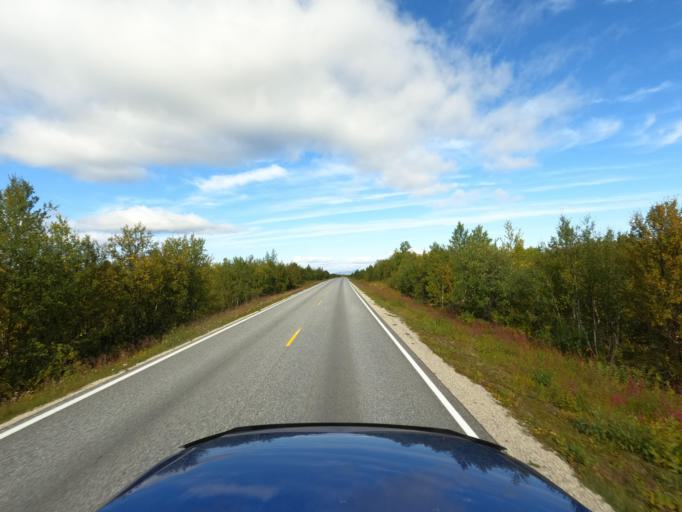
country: NO
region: Finnmark Fylke
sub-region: Karasjok
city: Karasjohka
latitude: 69.6550
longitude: 25.2780
